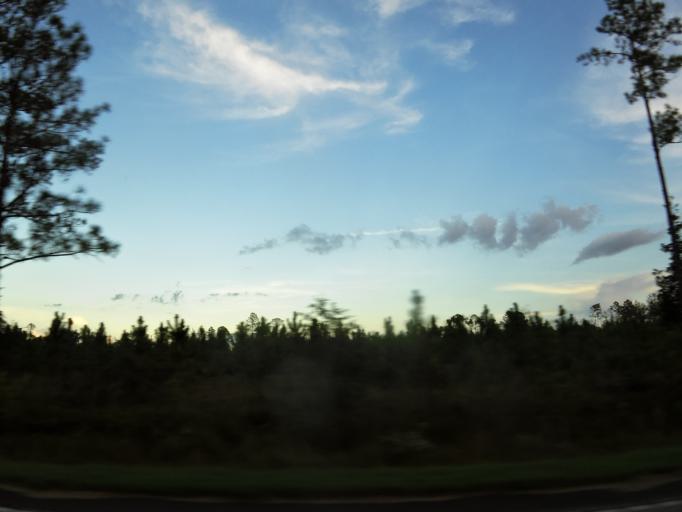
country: US
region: Georgia
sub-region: Echols County
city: Statenville
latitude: 30.6261
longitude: -83.0240
